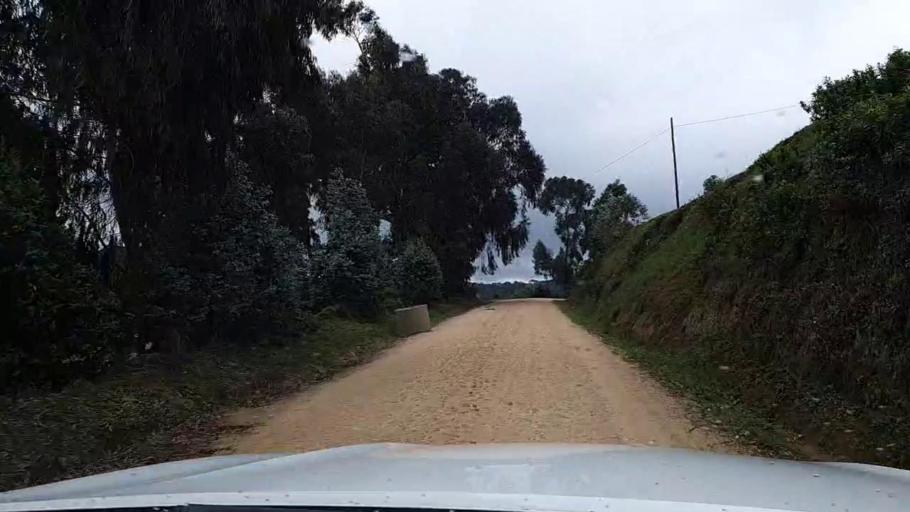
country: RW
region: Southern Province
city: Nzega
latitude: -2.3743
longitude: 29.3808
